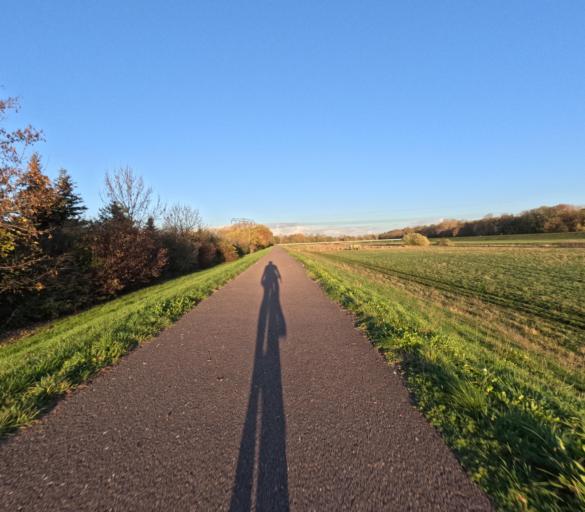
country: DE
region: Saxony-Anhalt
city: Ermlitz
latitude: 51.3857
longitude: 12.1487
